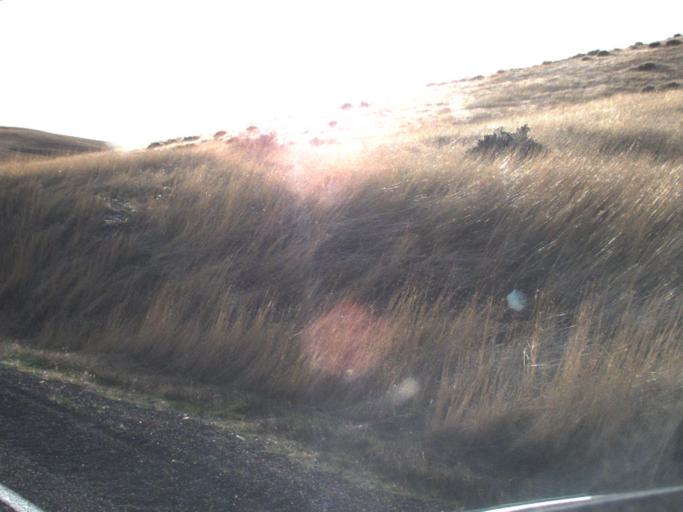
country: US
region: Washington
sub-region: Columbia County
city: Dayton
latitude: 46.4724
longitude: -117.9619
